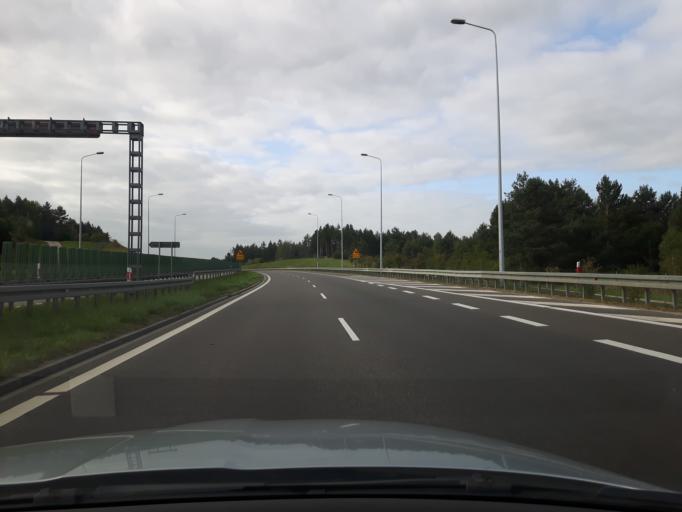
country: PL
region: Swietokrzyskie
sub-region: Powiat skarzyski
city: Suchedniow
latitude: 51.0446
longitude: 20.8190
